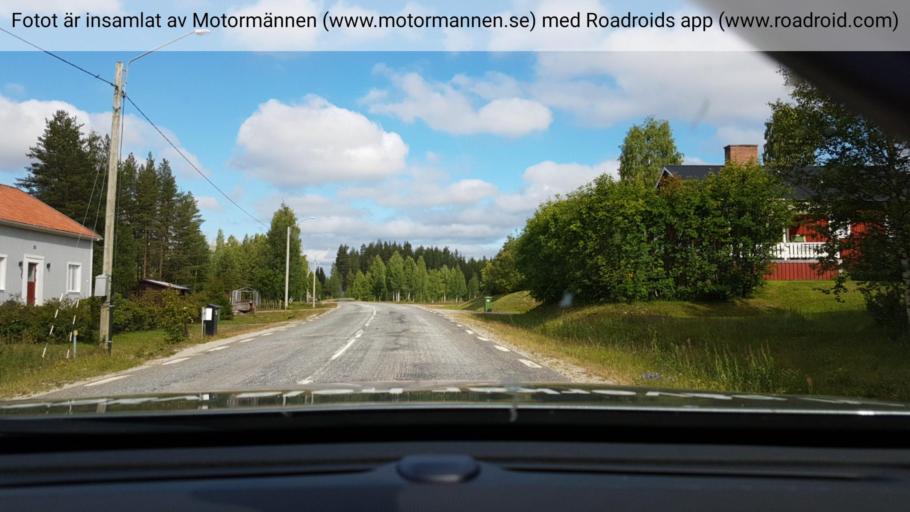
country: SE
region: Vaesterbotten
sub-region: Lycksele Kommun
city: Lycksele
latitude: 64.7666
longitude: 19.0429
